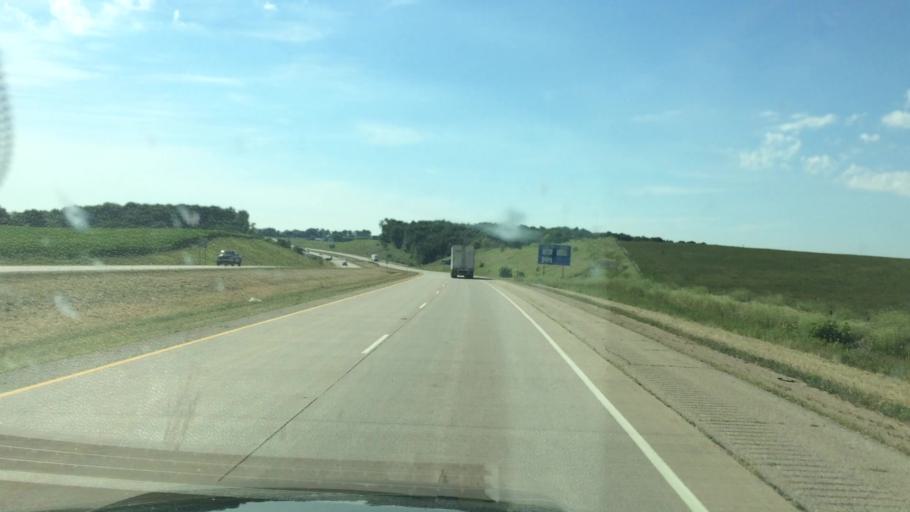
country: US
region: Wisconsin
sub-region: Shawano County
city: Bonduel
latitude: 44.7340
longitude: -88.4611
